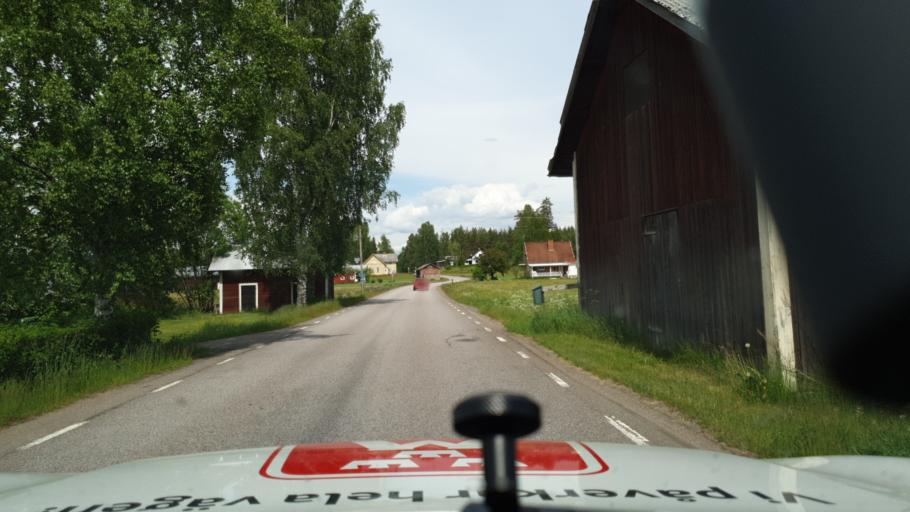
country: SE
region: Vaermland
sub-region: Torsby Kommun
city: Torsby
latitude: 59.9842
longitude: 12.8742
